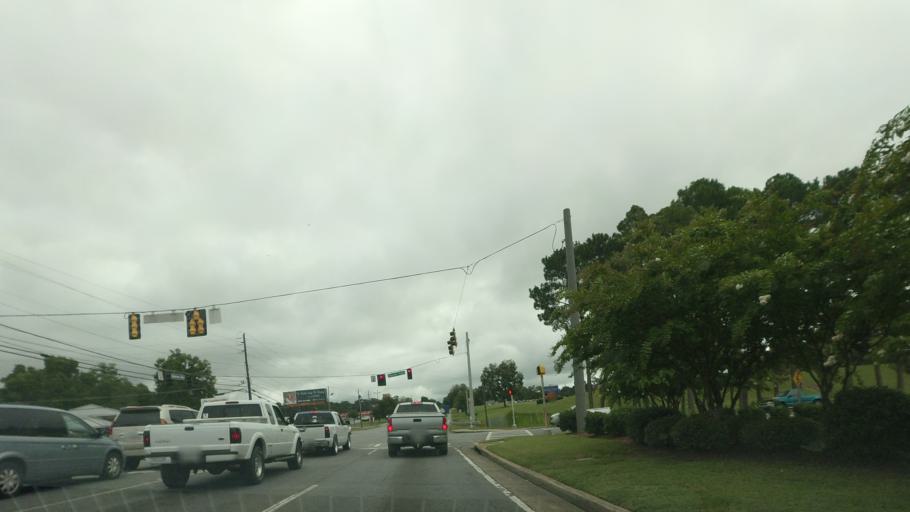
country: US
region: Georgia
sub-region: Laurens County
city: Dublin
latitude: 32.5408
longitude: -82.9474
